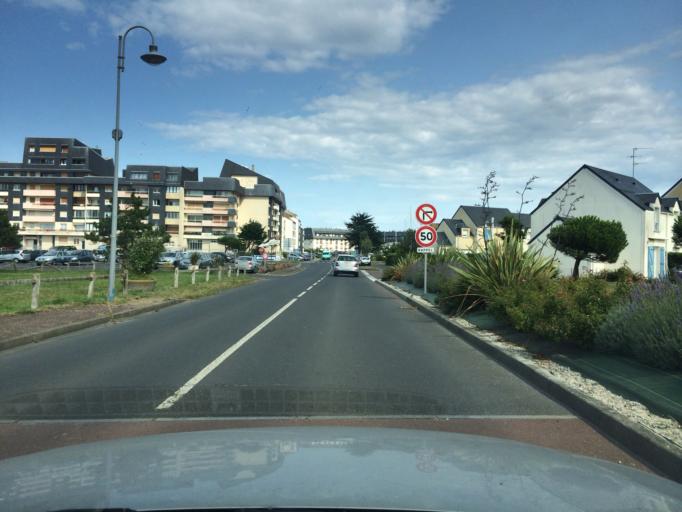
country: FR
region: Lower Normandy
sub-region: Departement du Calvados
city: Courseulles-sur-Mer
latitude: 49.3348
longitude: -0.4670
